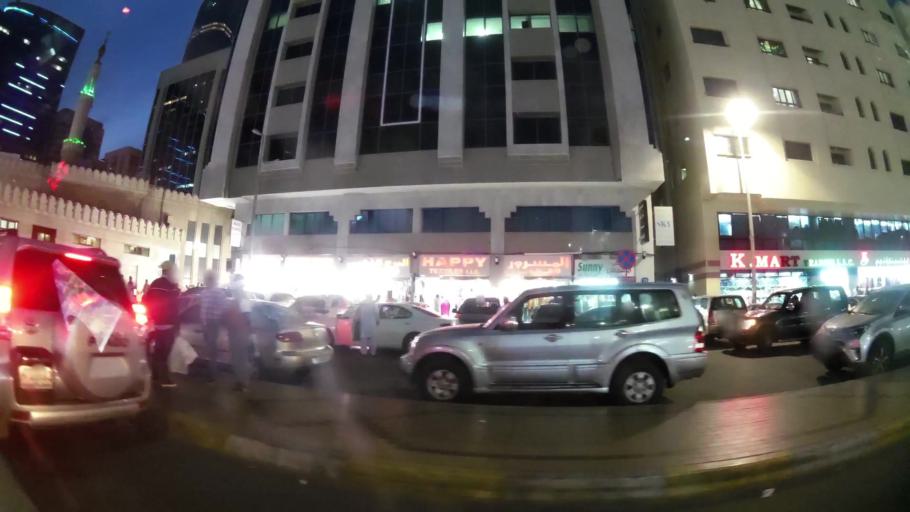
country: AE
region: Abu Dhabi
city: Abu Dhabi
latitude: 24.4866
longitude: 54.3610
